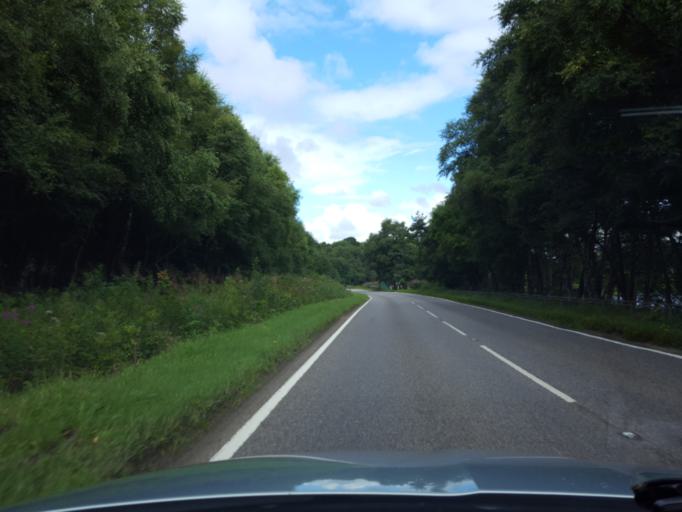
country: GB
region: Scotland
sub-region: Moray
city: Rothes
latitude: 57.5071
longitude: -3.1993
